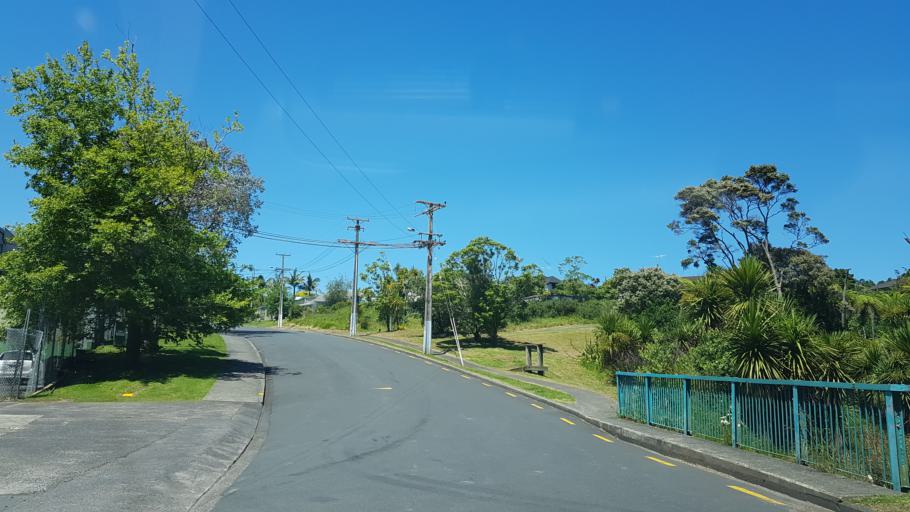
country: NZ
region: Auckland
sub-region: Auckland
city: North Shore
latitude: -36.8054
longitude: 174.7408
